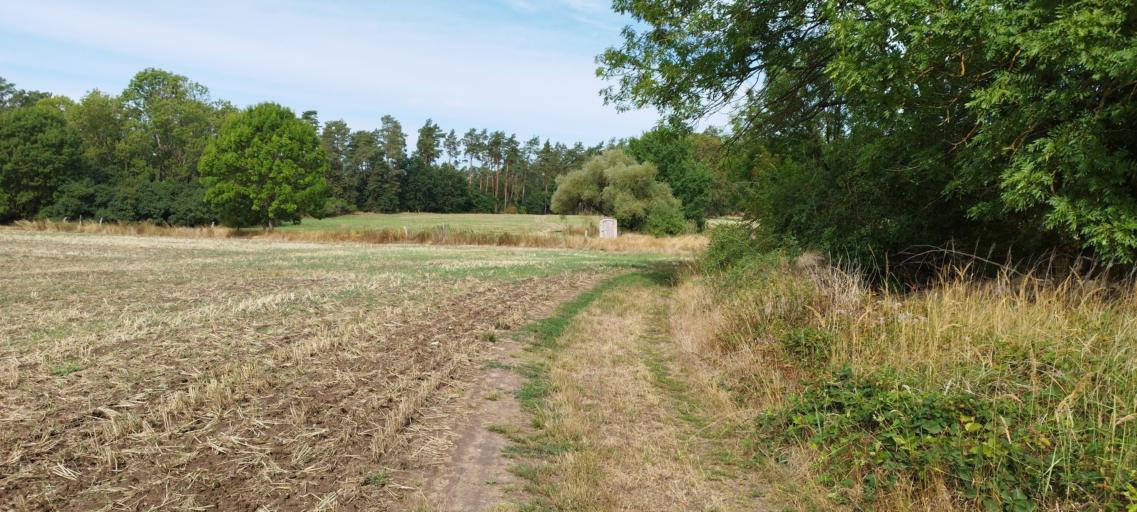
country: DE
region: Brandenburg
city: Wiesenburg
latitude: 52.1223
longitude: 12.5052
